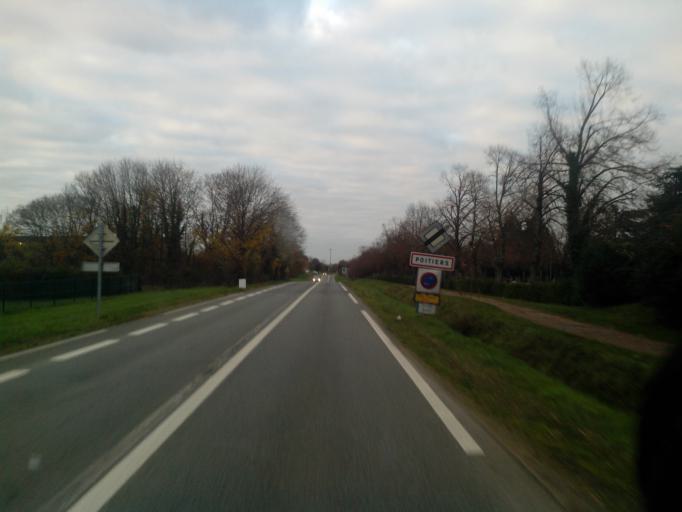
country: FR
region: Poitou-Charentes
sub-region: Departement de la Vienne
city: Mignaloux-Beauvoir
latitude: 46.5665
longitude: 0.3938
